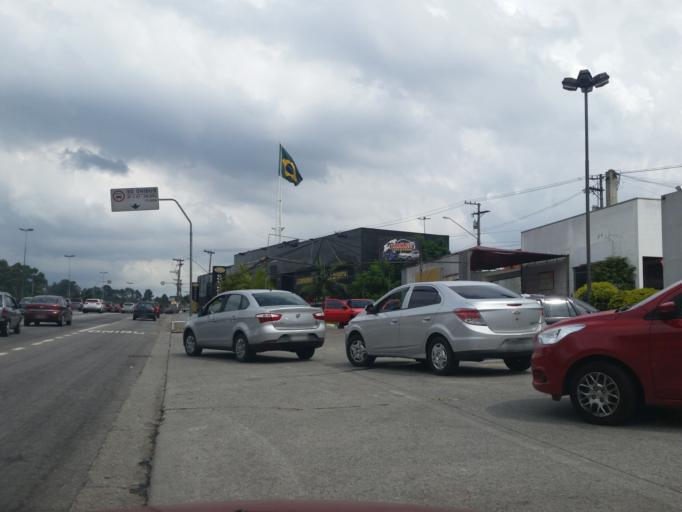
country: BR
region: Sao Paulo
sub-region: Ferraz De Vasconcelos
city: Ferraz de Vasconcelos
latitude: -23.5589
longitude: -46.4459
